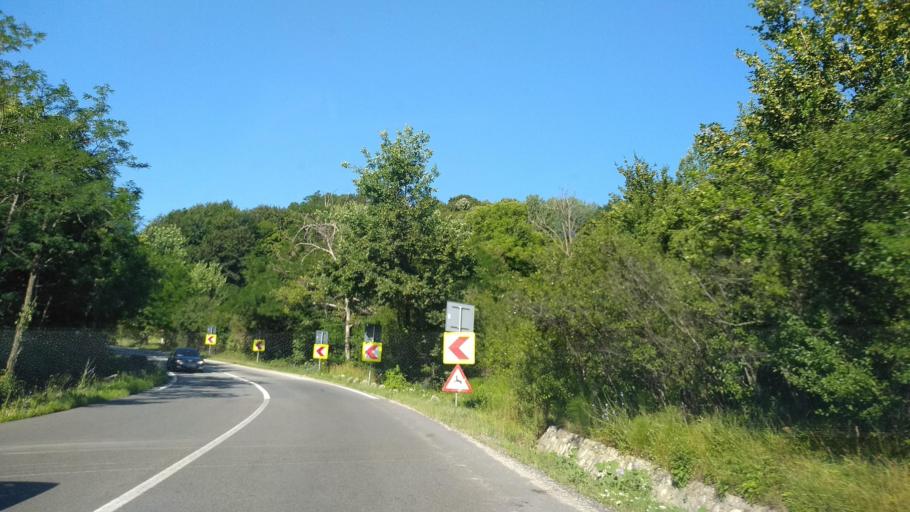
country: RO
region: Valcea
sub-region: Comuna Pietrari
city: Pietrari
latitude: 45.1090
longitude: 24.1383
